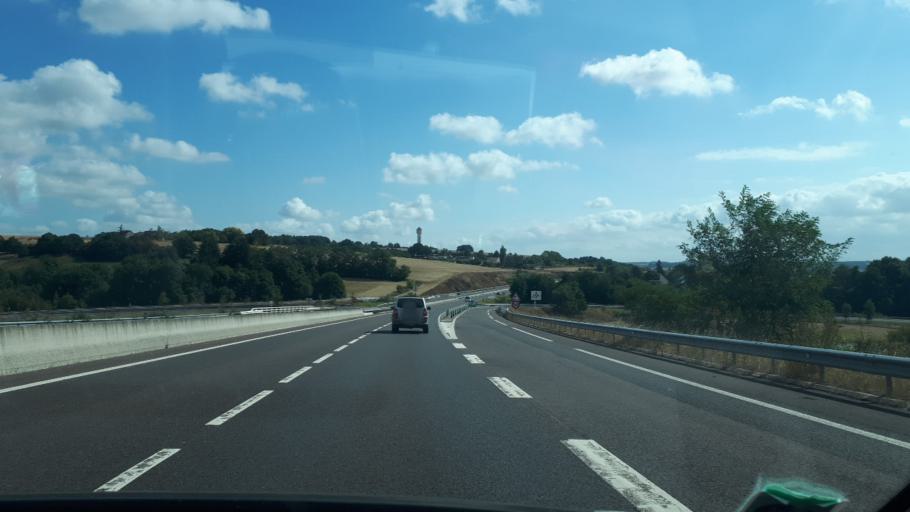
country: FR
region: Centre
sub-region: Departement du Loir-et-Cher
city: La Ville-aux-Clercs
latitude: 47.8731
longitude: 1.1361
